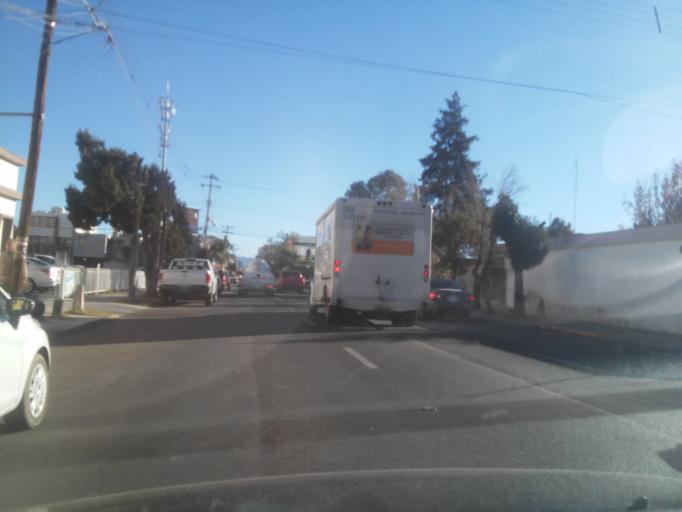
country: MX
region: Durango
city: Victoria de Durango
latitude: 24.0335
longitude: -104.6572
